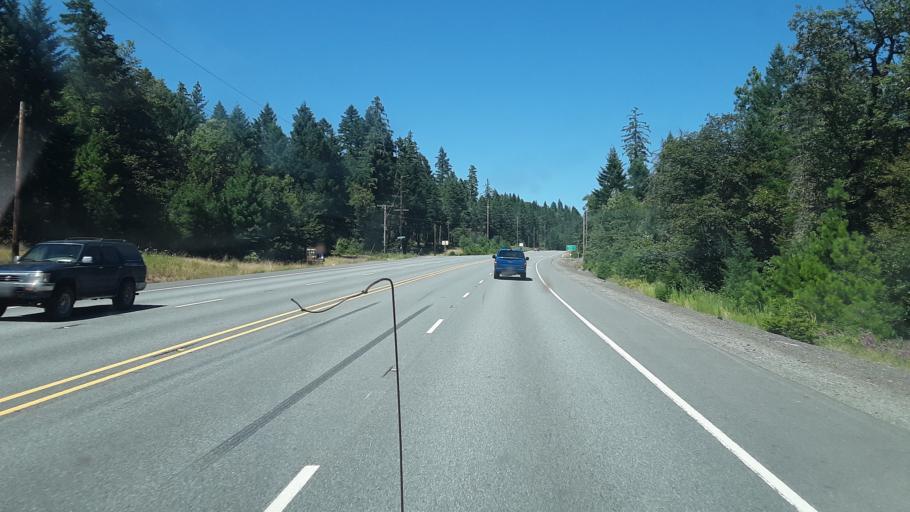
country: US
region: Oregon
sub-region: Josephine County
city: Cave Junction
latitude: 42.3281
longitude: -123.5931
